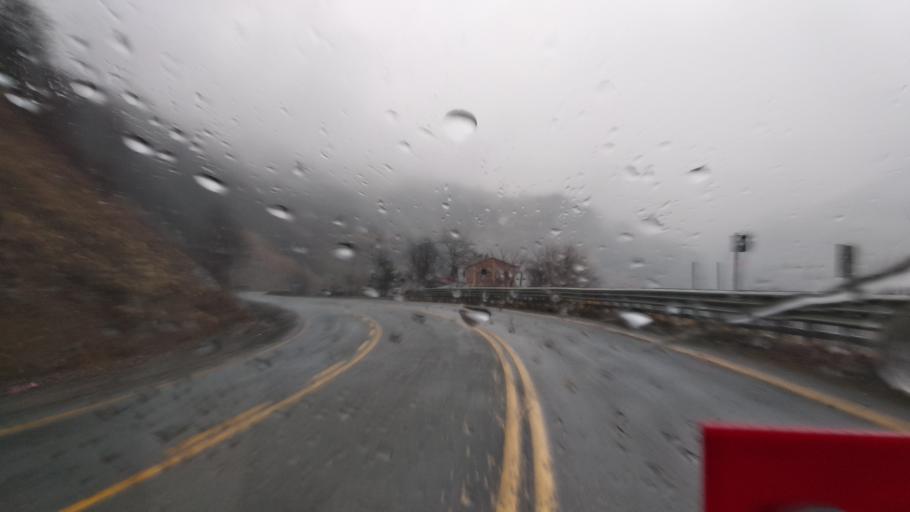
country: TR
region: Trabzon
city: Macka
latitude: 40.7048
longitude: 39.4916
